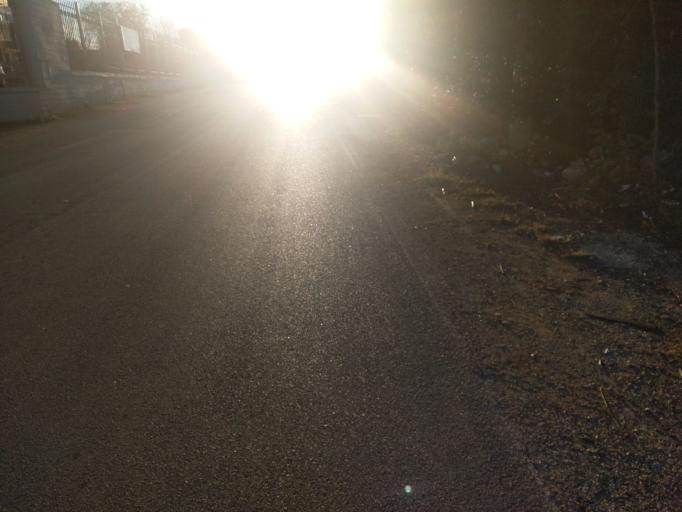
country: IT
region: Apulia
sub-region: Provincia di Bari
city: Bari
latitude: 41.1098
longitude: 16.8382
